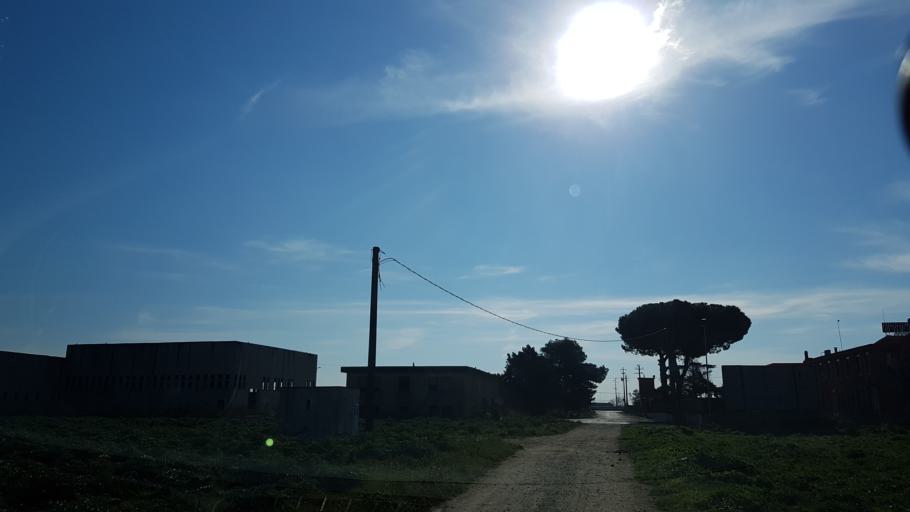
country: IT
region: Apulia
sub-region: Provincia di Brindisi
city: Brindisi
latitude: 40.6098
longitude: 17.8867
